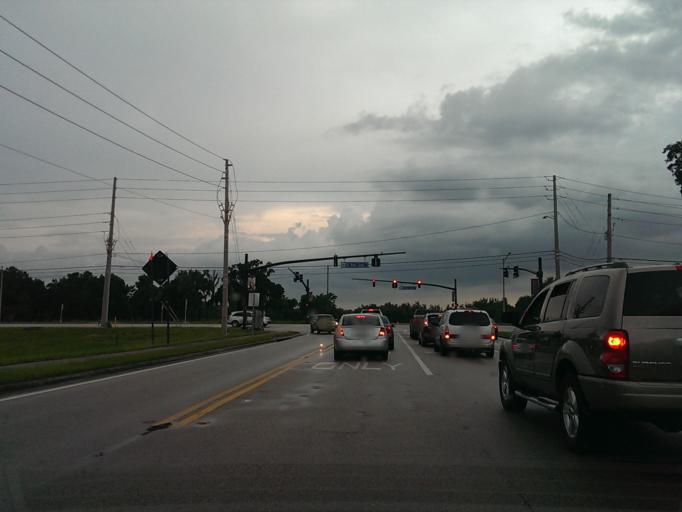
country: US
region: Florida
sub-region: Orange County
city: Ocoee
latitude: 28.5488
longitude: -81.5355
